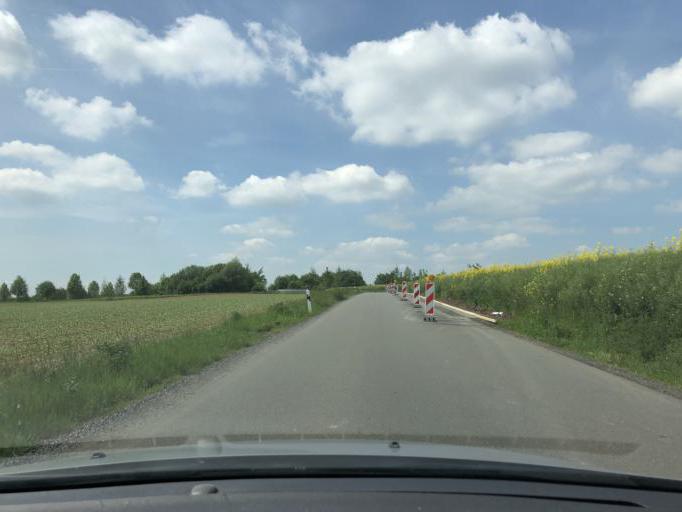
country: DE
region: Thuringia
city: Saara
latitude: 50.9590
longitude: 12.4179
